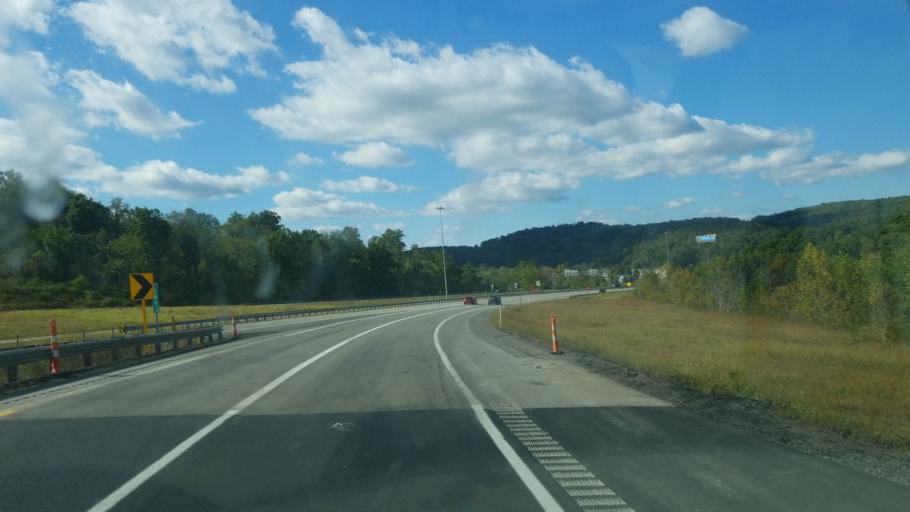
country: US
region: West Virginia
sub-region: Monongalia County
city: Morgantown
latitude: 39.5805
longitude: -79.9770
